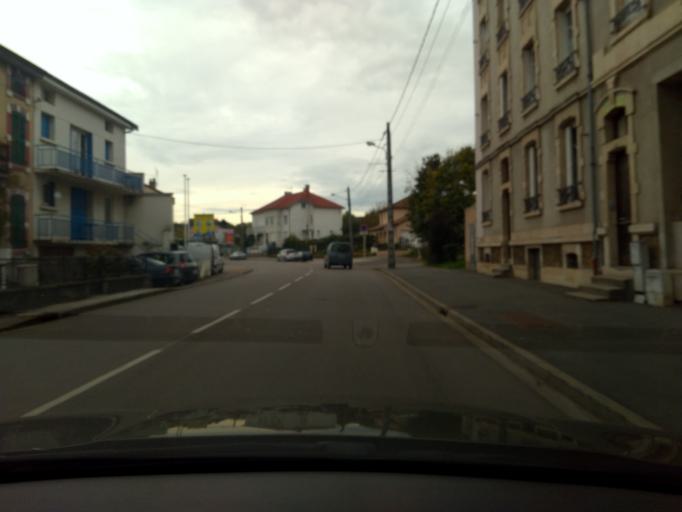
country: FR
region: Lorraine
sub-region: Departement de Meurthe-et-Moselle
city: Toul
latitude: 48.6681
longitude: 5.8822
